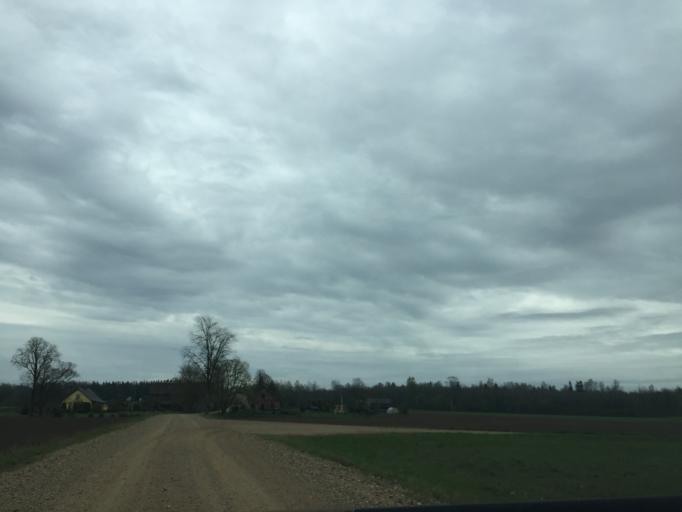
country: LV
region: Sigulda
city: Sigulda
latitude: 57.0364
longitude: 24.8476
